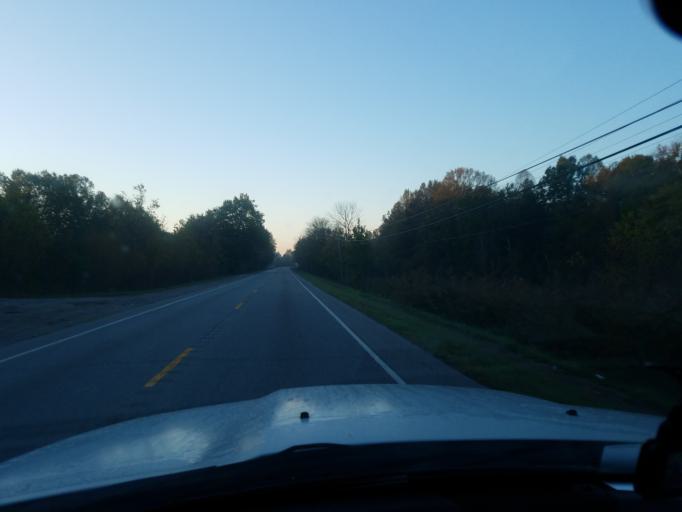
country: US
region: Kentucky
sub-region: Laurel County
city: London
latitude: 37.0783
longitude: -84.0592
